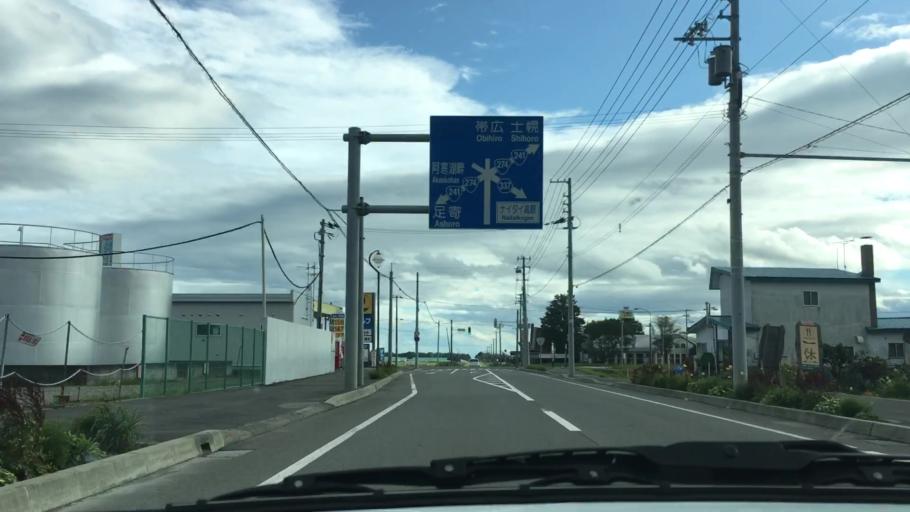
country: JP
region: Hokkaido
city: Otofuke
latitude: 43.2260
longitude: 143.2936
